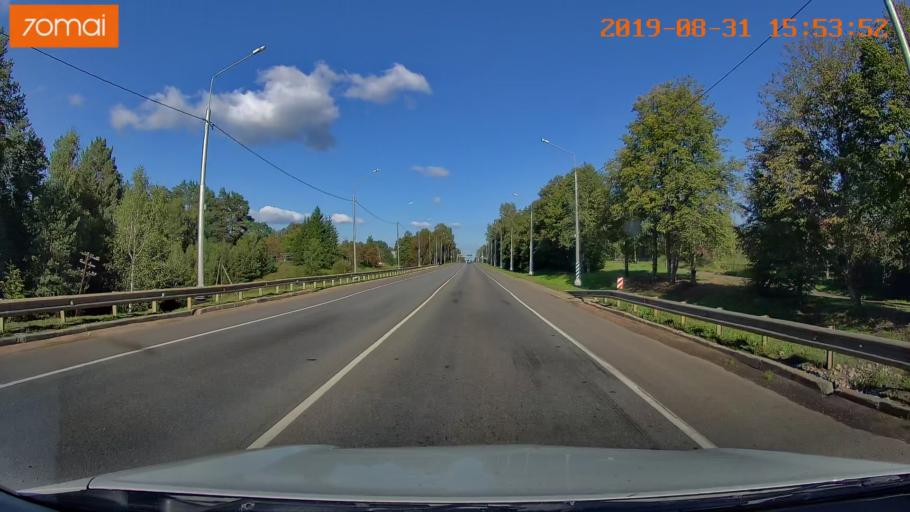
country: RU
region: Kaluga
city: Yukhnov
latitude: 54.7153
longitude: 35.1394
